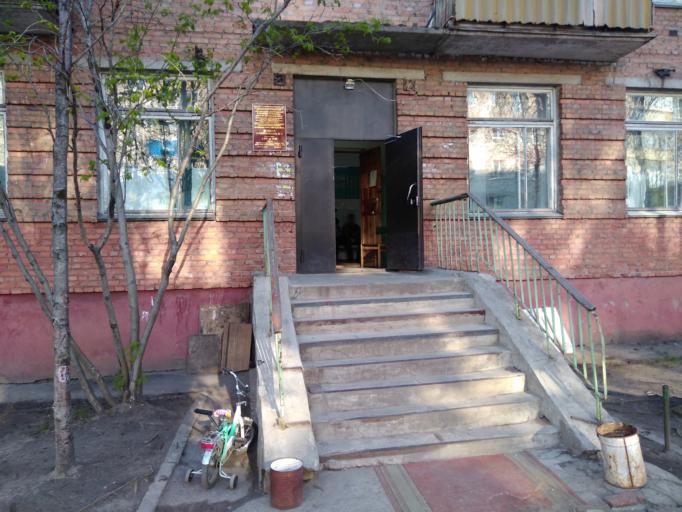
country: RU
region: Komi Republic
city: Pechora
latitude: 65.1085
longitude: 57.1542
